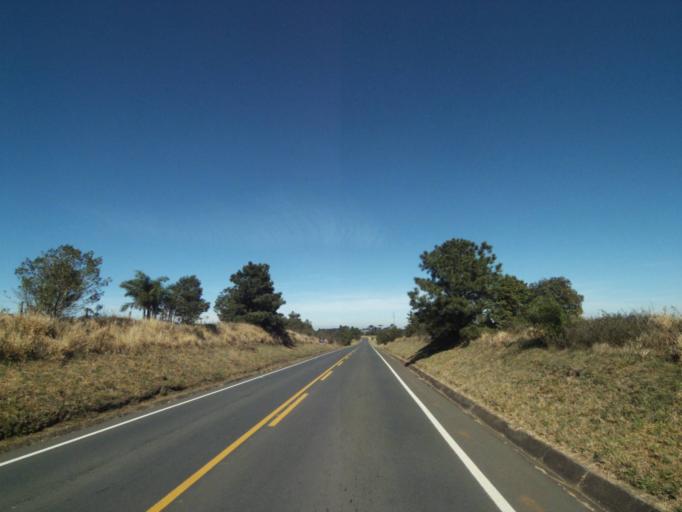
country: BR
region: Parana
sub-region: Castro
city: Castro
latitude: -24.7407
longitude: -50.1830
